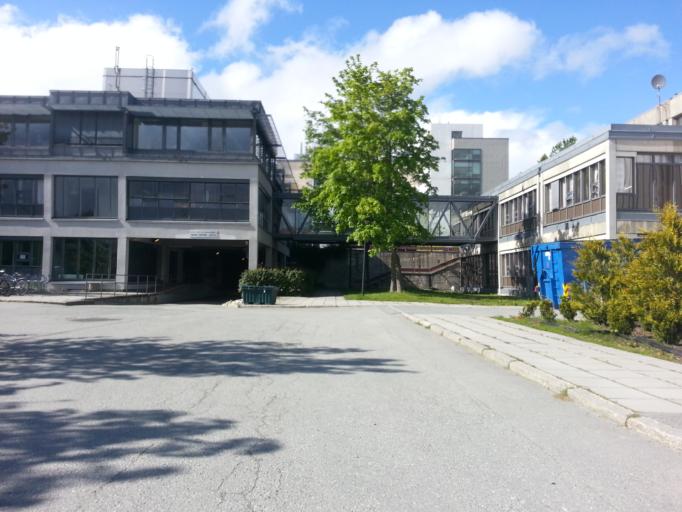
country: NO
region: Sor-Trondelag
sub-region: Trondheim
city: Trondheim
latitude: 63.4142
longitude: 10.4079
